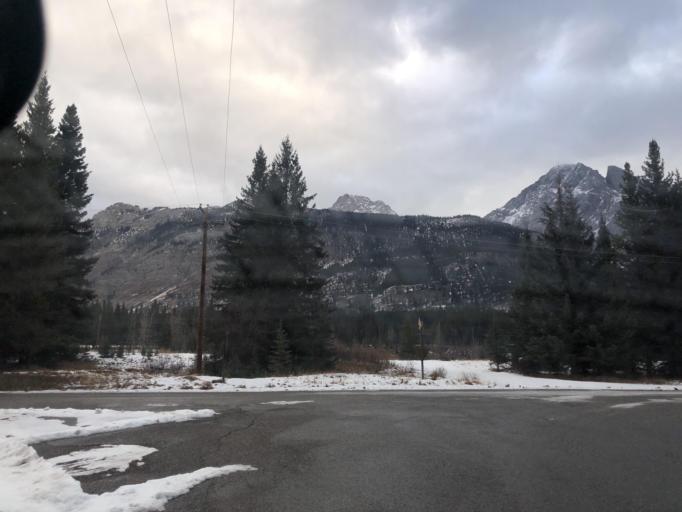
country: CA
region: Alberta
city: Canmore
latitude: 50.7148
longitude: -115.1214
